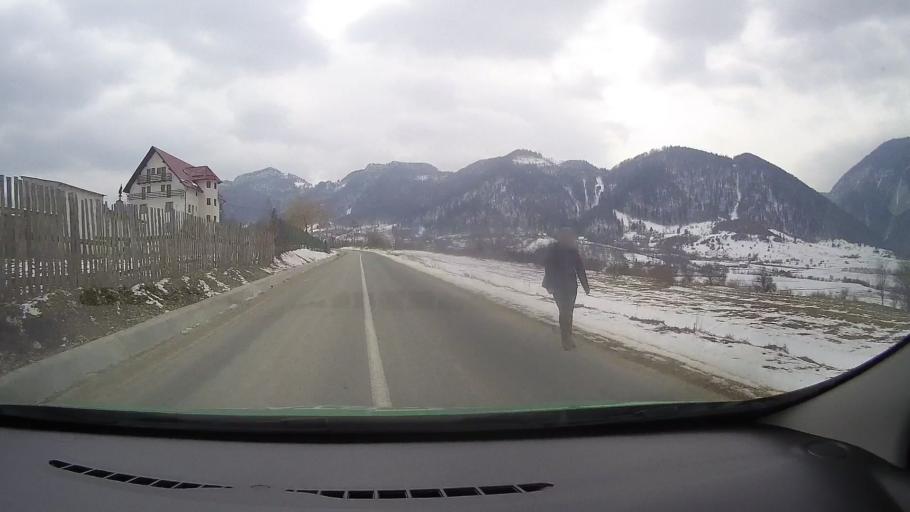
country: RO
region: Brasov
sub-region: Comuna Zarnesti
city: Zarnesti
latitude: 45.5497
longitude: 25.3220
